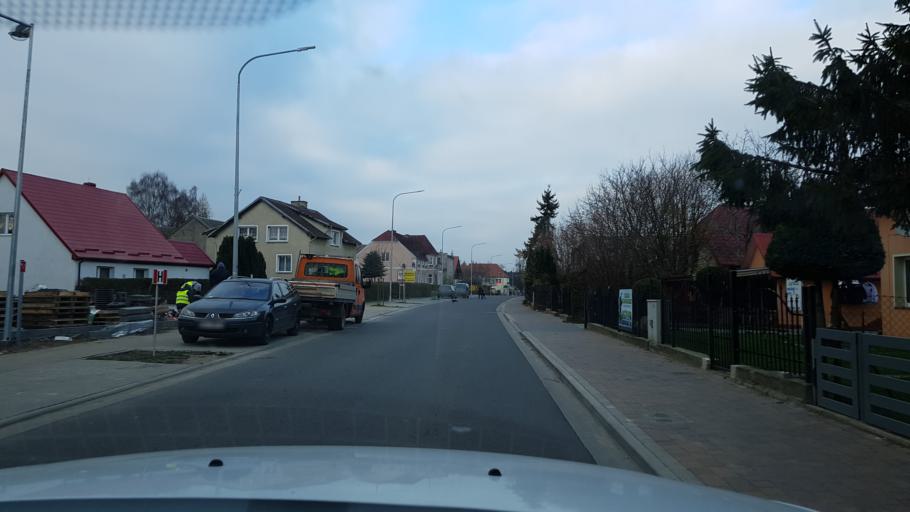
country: PL
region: West Pomeranian Voivodeship
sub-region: Powiat kolobrzeski
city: Goscino
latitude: 54.0505
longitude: 15.6534
